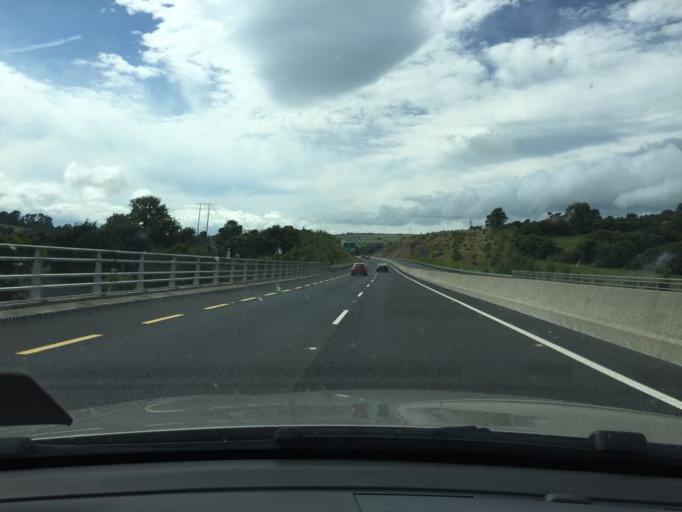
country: IE
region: Leinster
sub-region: Kilkenny
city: Mooncoin
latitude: 52.2388
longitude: -7.2389
